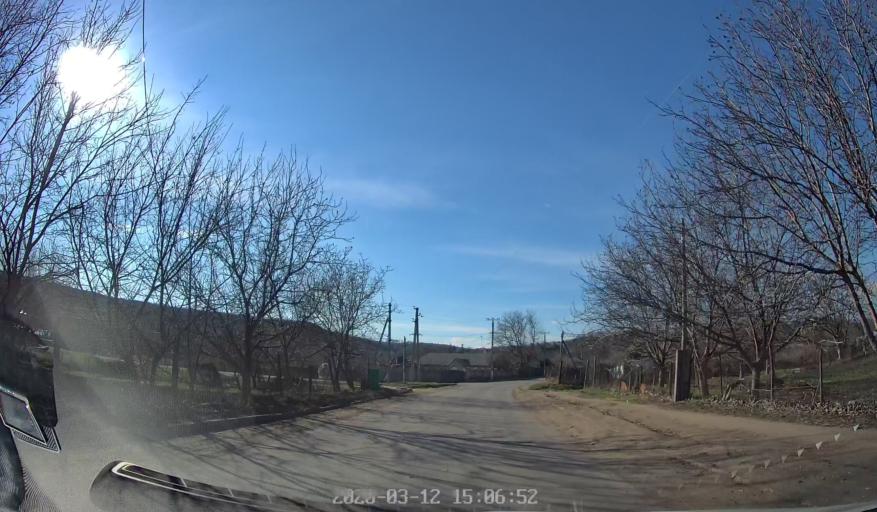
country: MD
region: Telenesti
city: Cocieri
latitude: 47.2201
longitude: 29.0071
